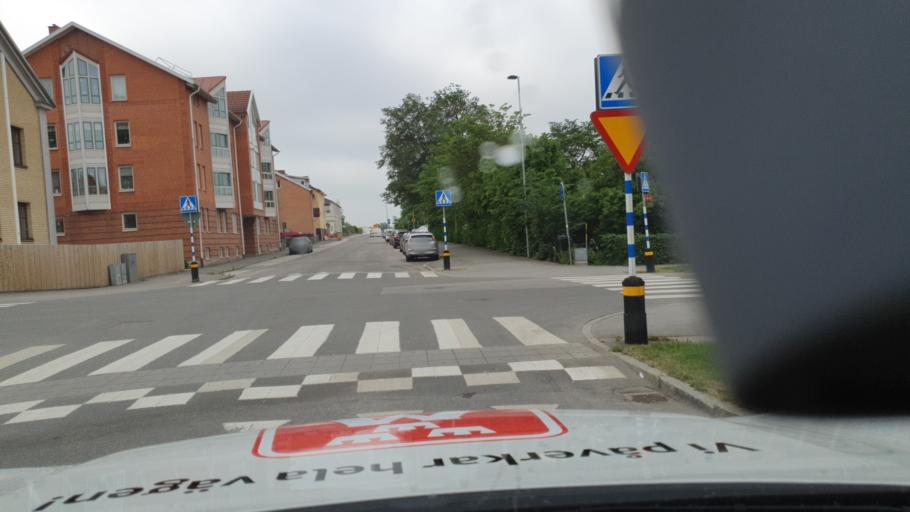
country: SE
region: Vaestra Goetaland
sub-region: Falkopings Kommun
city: Falkoeping
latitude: 58.1633
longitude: 13.5492
